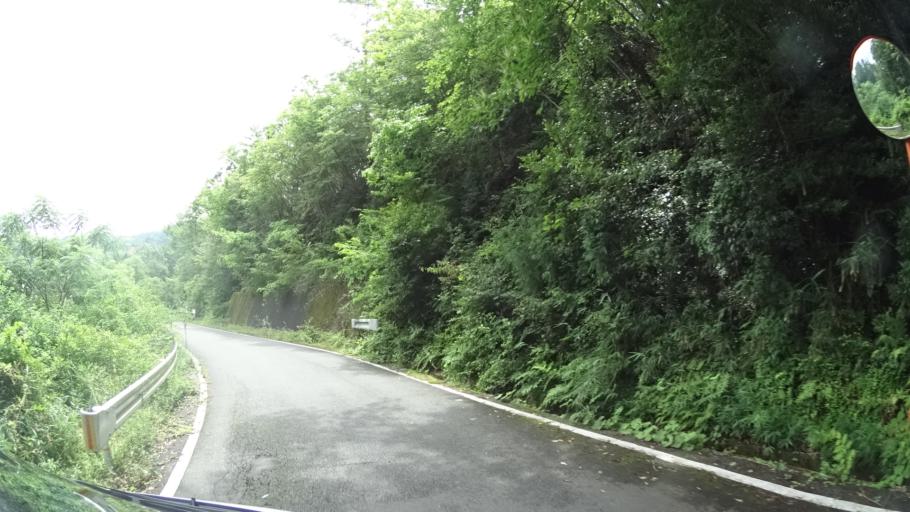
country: JP
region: Kyoto
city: Kameoka
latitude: 35.0889
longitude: 135.4533
